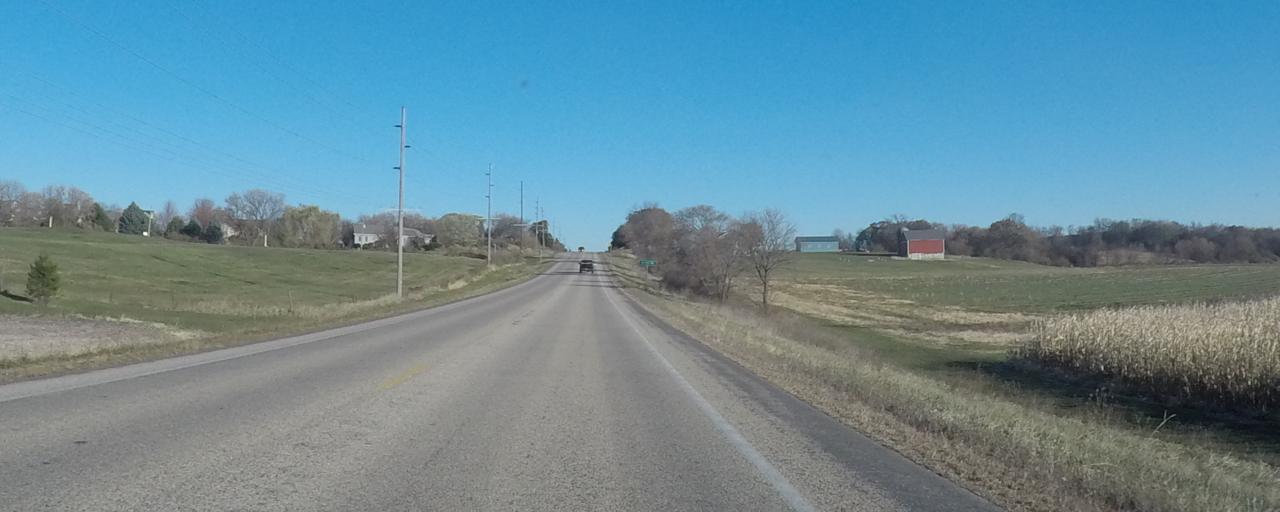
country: US
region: Wisconsin
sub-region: Dane County
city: Cottage Grove
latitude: 43.0463
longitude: -89.1999
